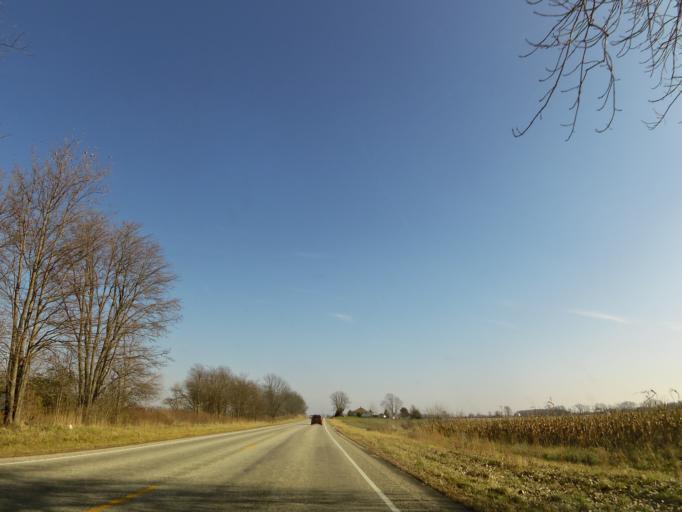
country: US
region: Indiana
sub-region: Rush County
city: Rushville
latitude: 39.5797
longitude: -85.5686
